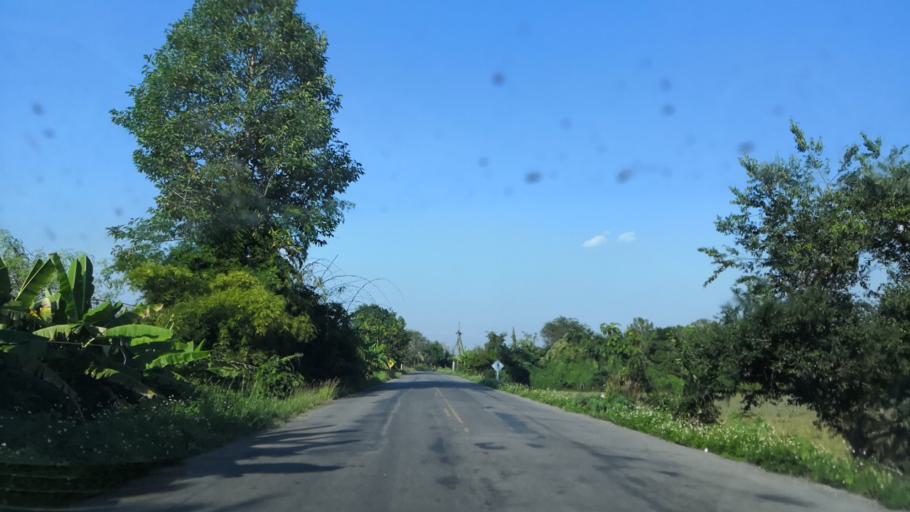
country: TH
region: Chiang Rai
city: Wiang Chai
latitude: 19.9440
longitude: 99.9170
